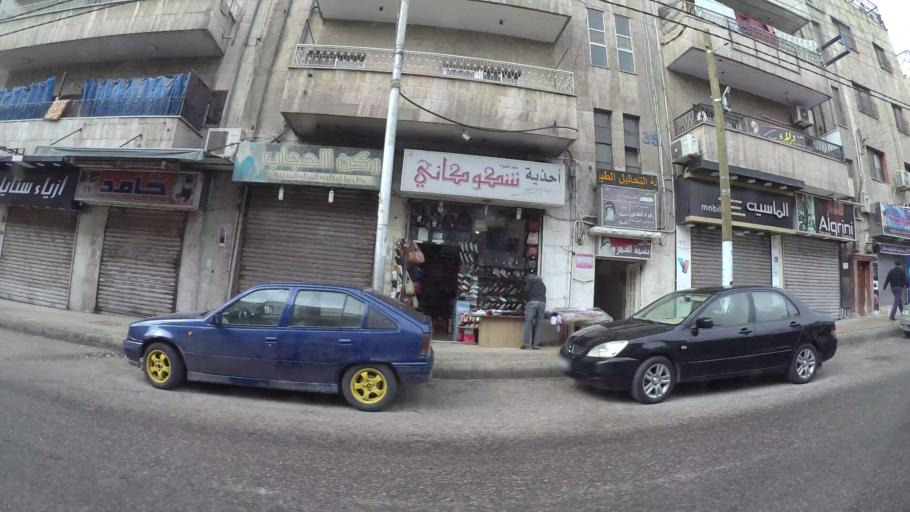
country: JO
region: Amman
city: Amman
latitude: 31.9745
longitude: 35.9259
